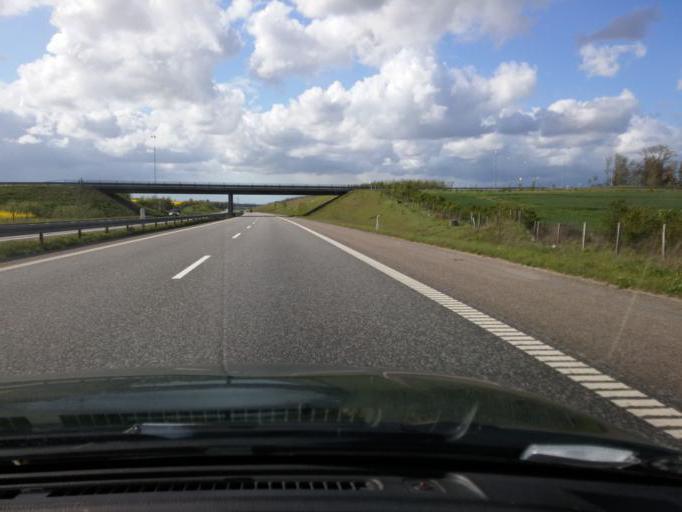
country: DK
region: South Denmark
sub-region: Faaborg-Midtfyn Kommune
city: Arslev
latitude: 55.2808
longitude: 10.4552
